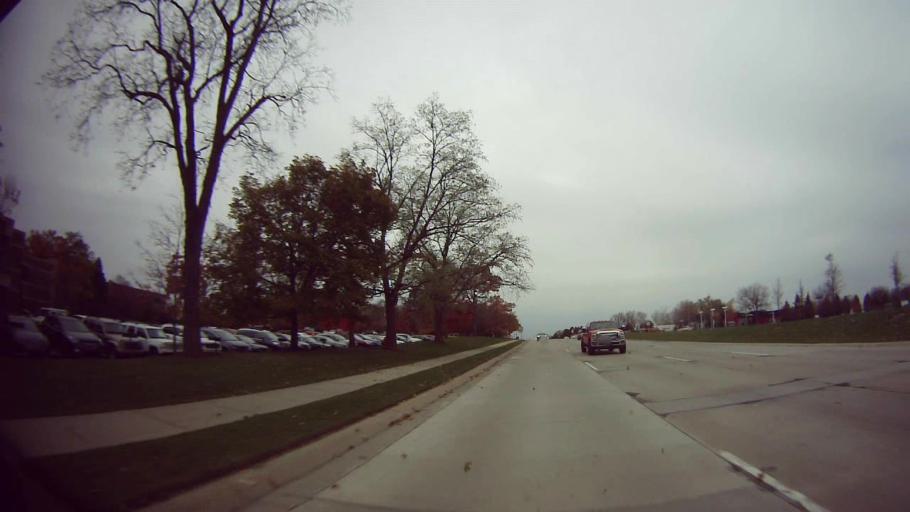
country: US
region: Michigan
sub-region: Oakland County
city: Sylvan Lake
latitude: 42.6134
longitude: -83.3088
